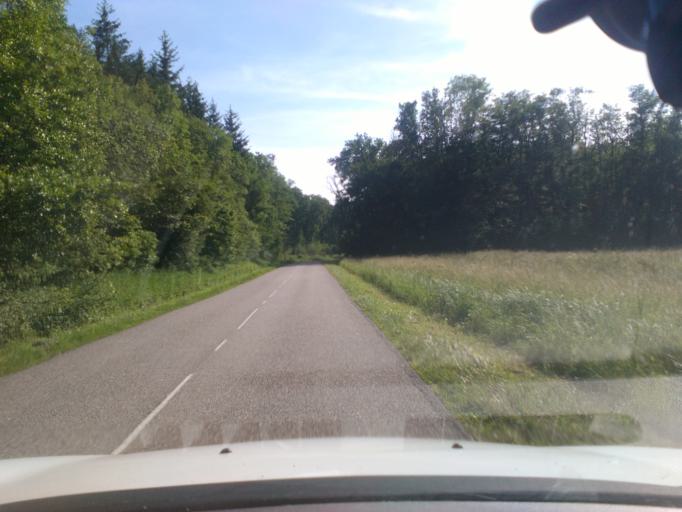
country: FR
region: Lorraine
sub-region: Departement des Vosges
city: Mirecourt
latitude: 48.2537
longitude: 6.2081
